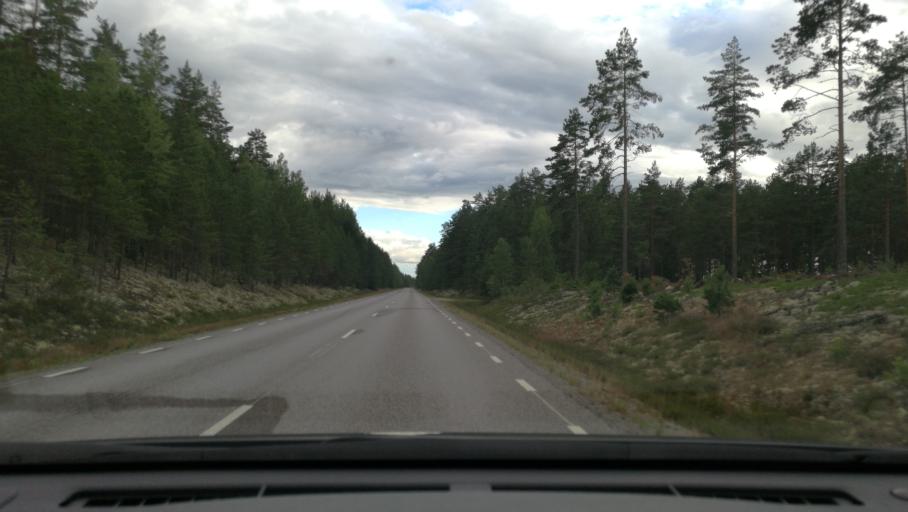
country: SE
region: OEstergoetland
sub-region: Norrkopings Kommun
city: Svartinge
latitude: 58.7376
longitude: 15.9569
